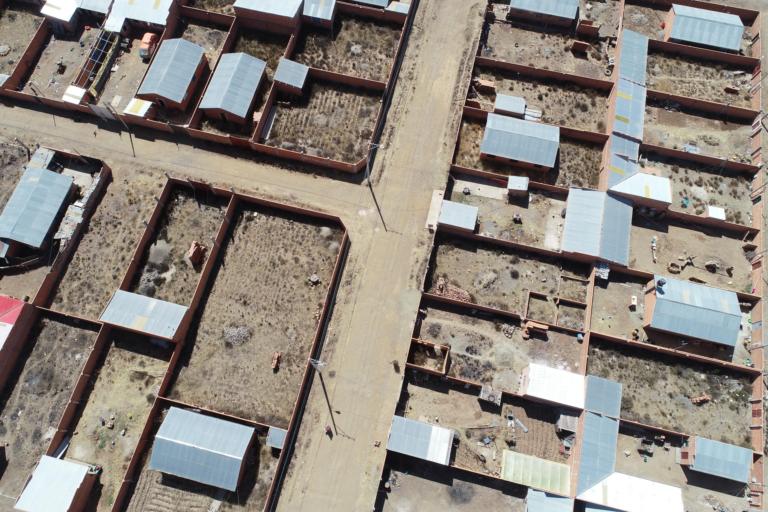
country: BO
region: La Paz
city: La Paz
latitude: -16.5942
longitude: -68.2109
